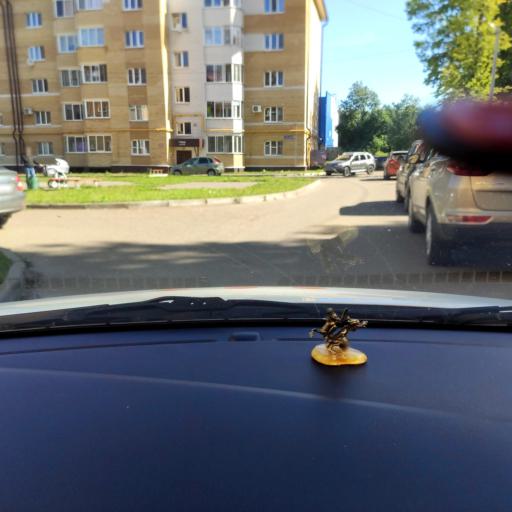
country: RU
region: Tatarstan
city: Vysokaya Gora
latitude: 55.9219
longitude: 49.3029
